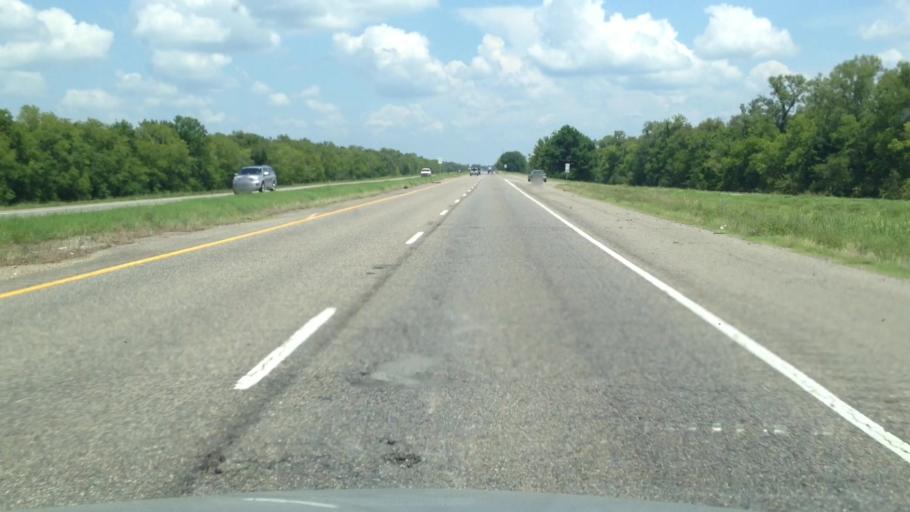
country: US
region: Louisiana
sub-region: Saint Landry Parish
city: Krotz Springs
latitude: 30.5450
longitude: -91.8090
